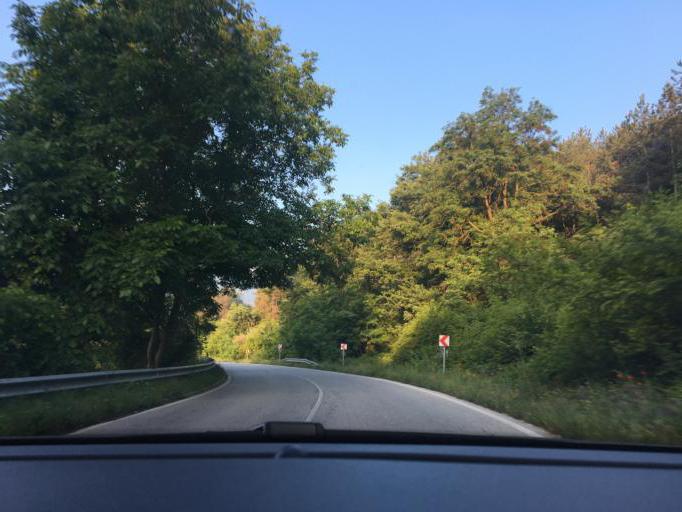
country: MK
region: Novo Selo
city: Novo Selo
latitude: 41.3975
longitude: 23.0295
